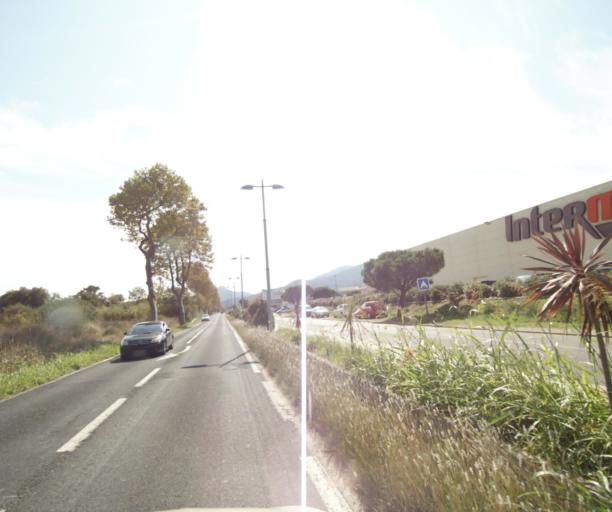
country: FR
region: Languedoc-Roussillon
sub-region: Departement des Pyrenees-Orientales
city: Argelers
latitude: 42.5589
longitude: 3.0102
